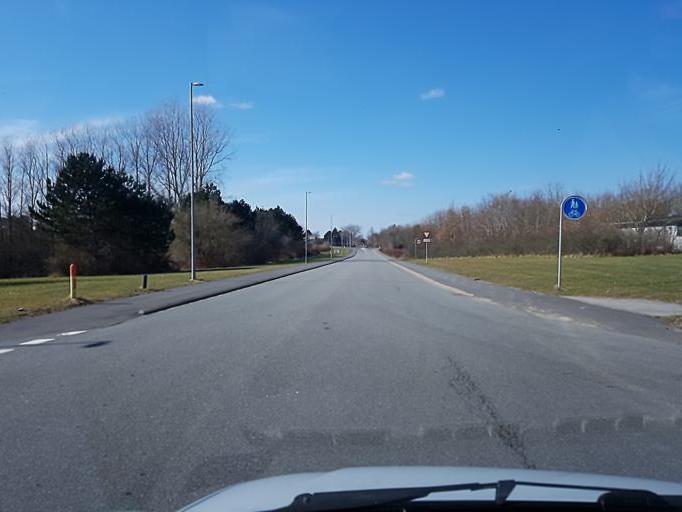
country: DK
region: South Denmark
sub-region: Varde Kommune
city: Varde
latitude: 55.6088
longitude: 8.5022
